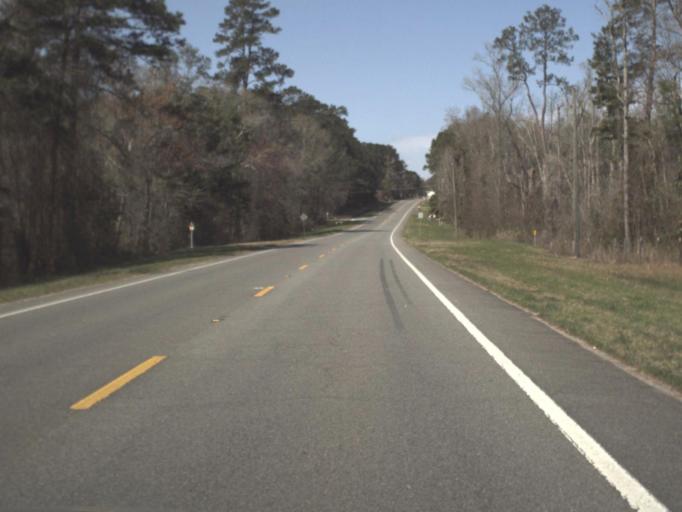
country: US
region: Florida
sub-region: Gadsden County
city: Quincy
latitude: 30.5943
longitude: -84.5295
